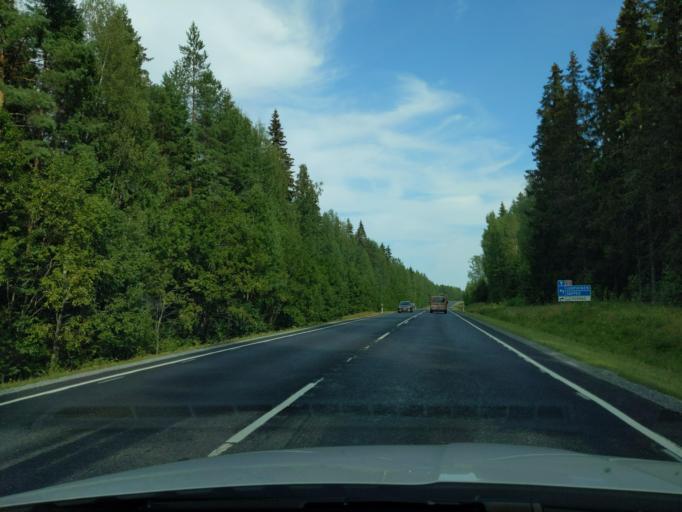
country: FI
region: Haeme
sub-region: Haemeenlinna
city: Hauho
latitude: 61.1733
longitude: 24.5999
